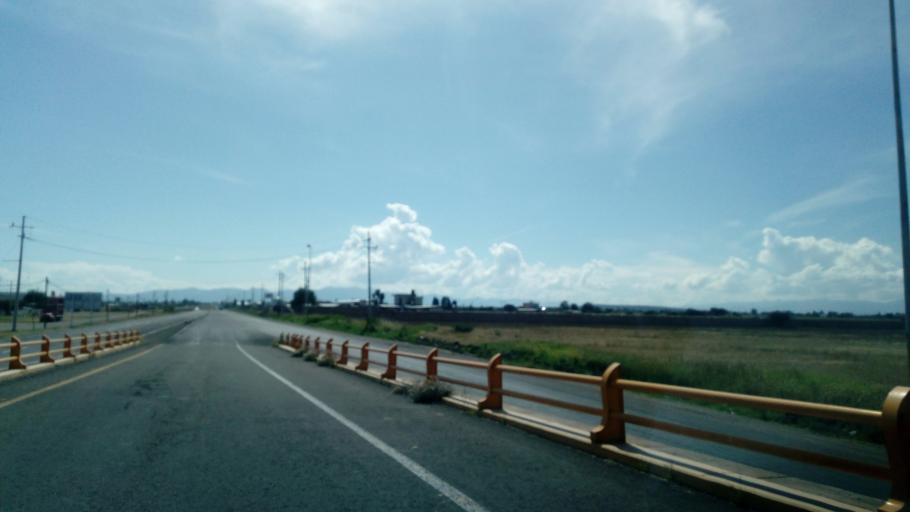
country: MX
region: Durango
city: Victoria de Durango
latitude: 24.0938
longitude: -104.5734
